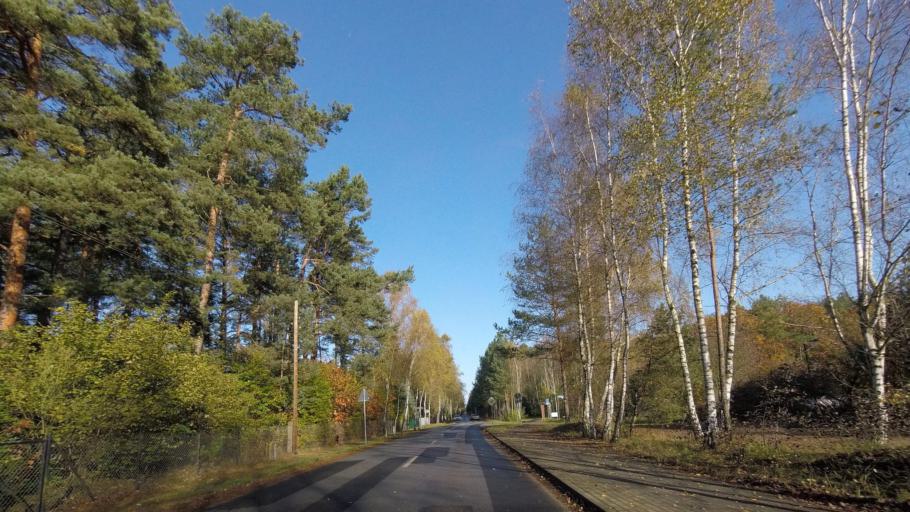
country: DE
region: Brandenburg
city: Borkwalde
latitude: 52.2536
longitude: 12.8352
